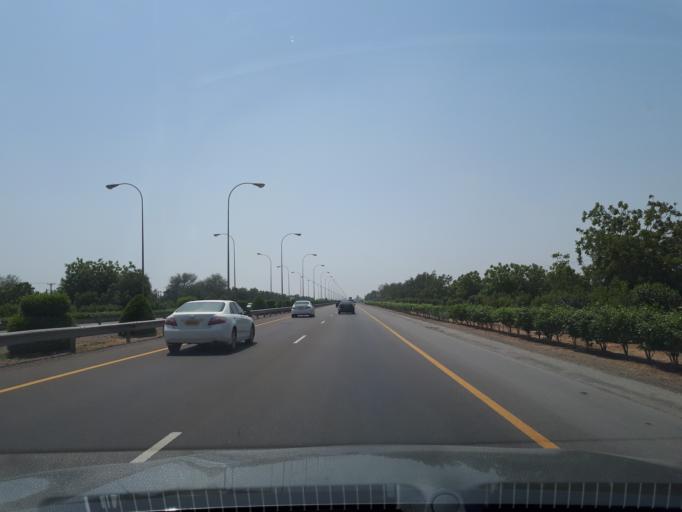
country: OM
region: Al Batinah
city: Al Sohar
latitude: 24.4003
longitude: 56.6645
